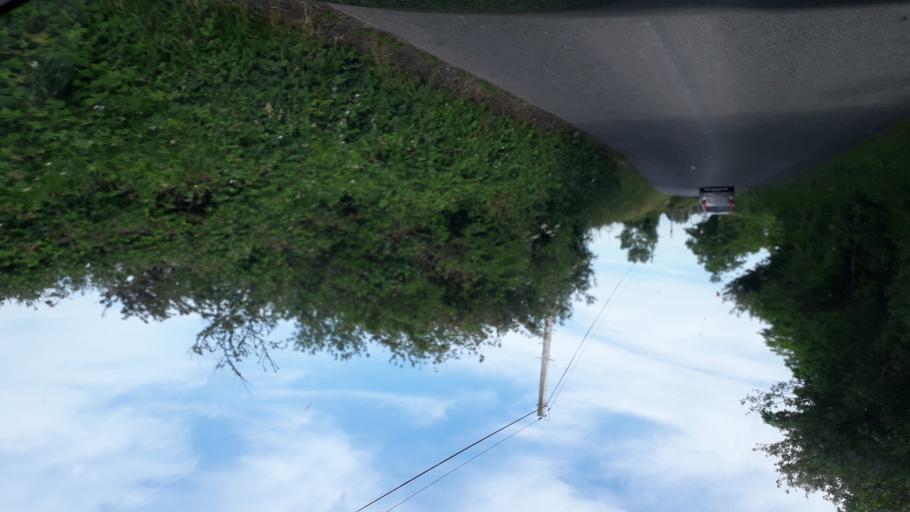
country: IE
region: Leinster
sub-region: Loch Garman
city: Courtown
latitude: 52.5274
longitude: -6.2688
